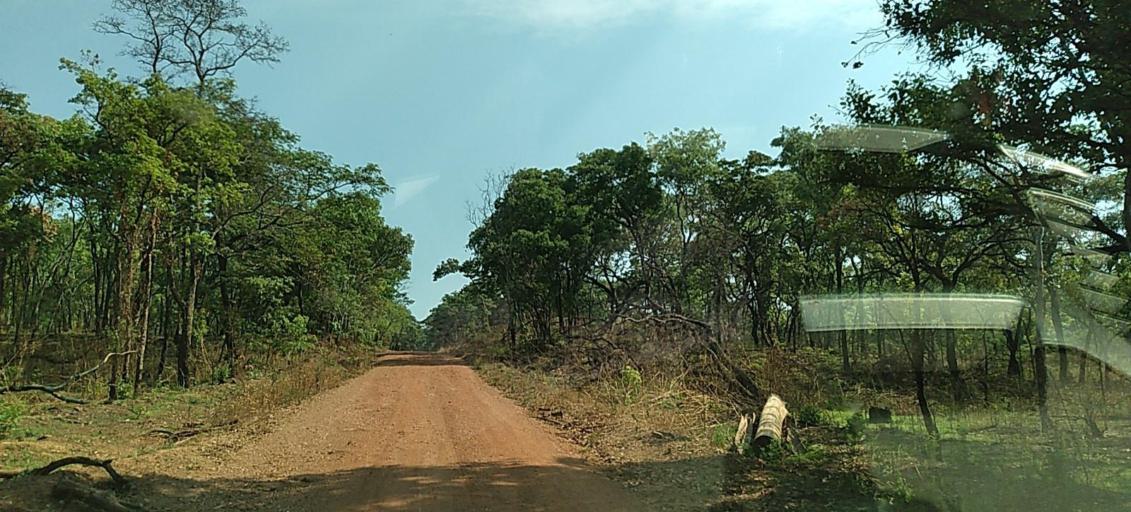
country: ZM
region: Copperbelt
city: Kalulushi
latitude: -12.9338
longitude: 27.8214
